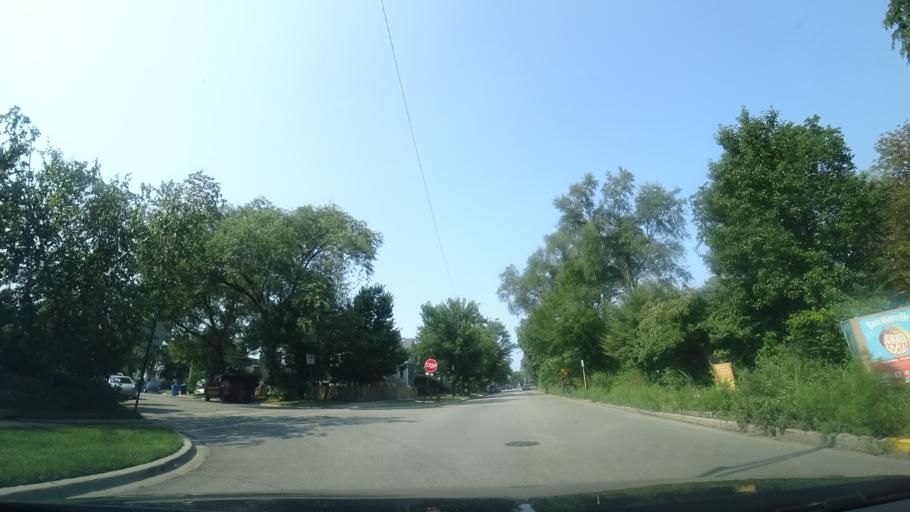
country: US
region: Illinois
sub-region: Cook County
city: Lincolnwood
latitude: 41.9796
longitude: -87.6843
